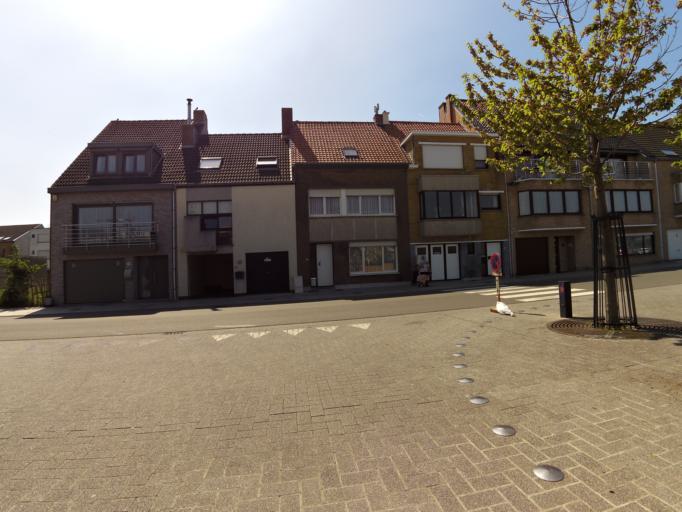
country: BE
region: Flanders
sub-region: Provincie West-Vlaanderen
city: Middelkerke
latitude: 51.1866
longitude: 2.8223
